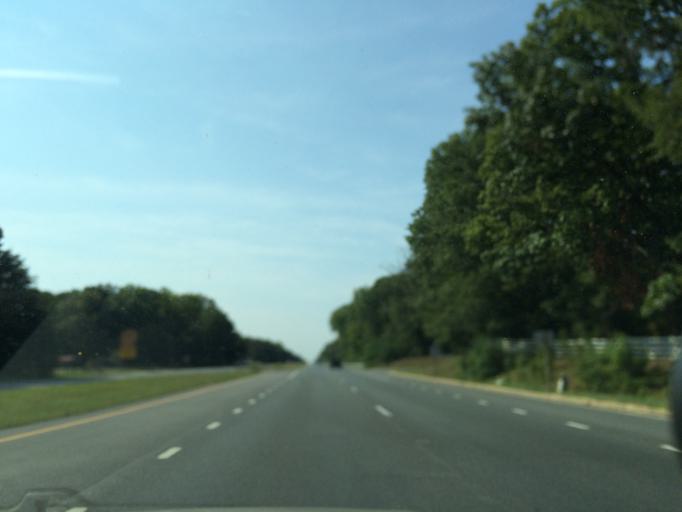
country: US
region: Maryland
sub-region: Charles County
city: La Plata
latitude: 38.4885
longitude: -76.9878
